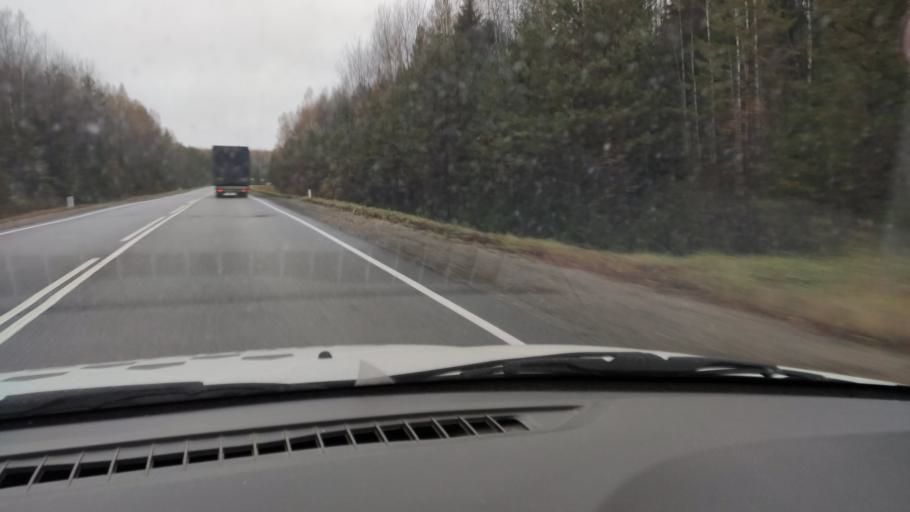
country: RU
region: Kirov
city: Chernaya Kholunitsa
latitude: 58.8291
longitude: 51.7676
